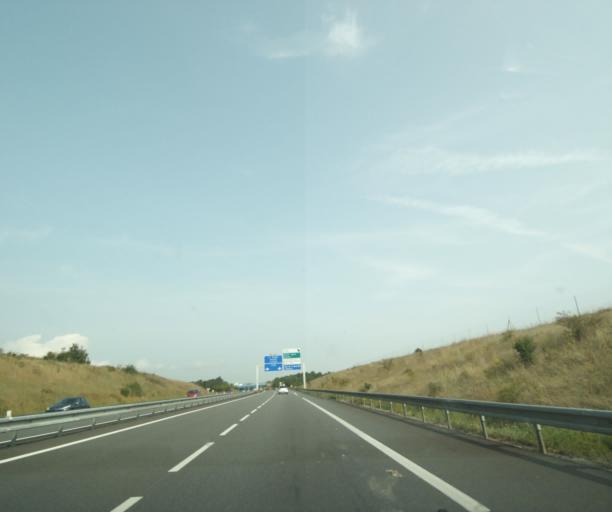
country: FR
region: Lower Normandy
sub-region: Departement de l'Orne
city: Valframbert
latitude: 48.4490
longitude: 0.1336
